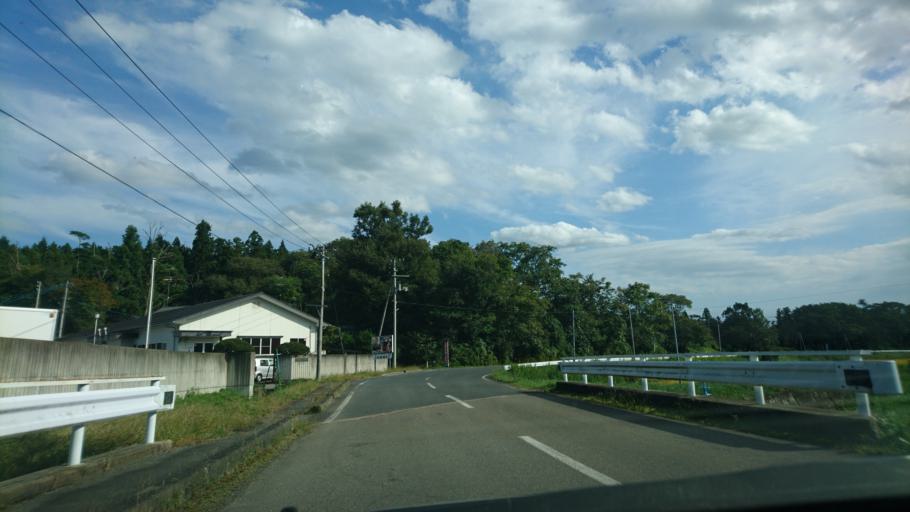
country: JP
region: Iwate
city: Ichinoseki
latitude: 38.8386
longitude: 141.1921
